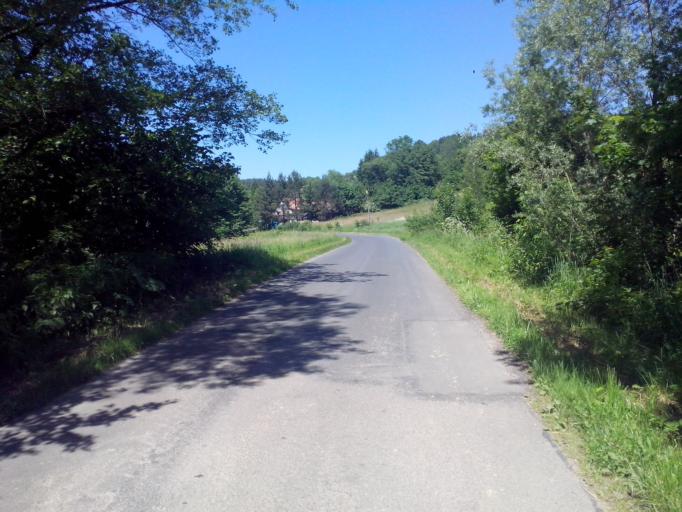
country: PL
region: Subcarpathian Voivodeship
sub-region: Powiat krosnienski
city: Wojaszowka
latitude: 49.7996
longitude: 21.7018
